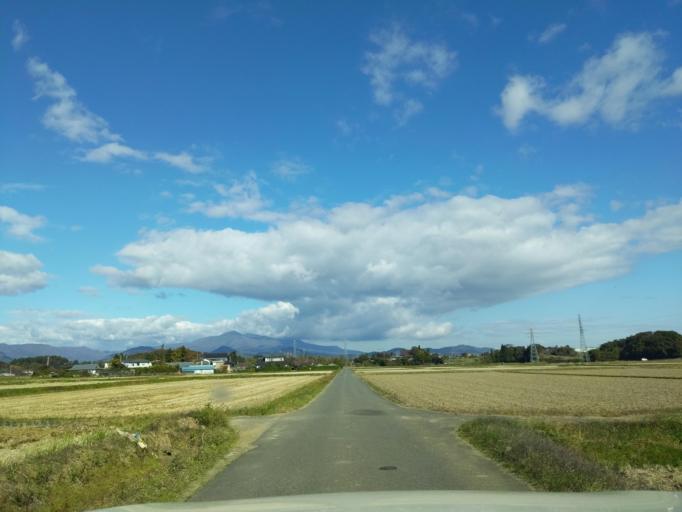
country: JP
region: Fukushima
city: Koriyama
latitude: 37.4236
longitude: 140.3288
